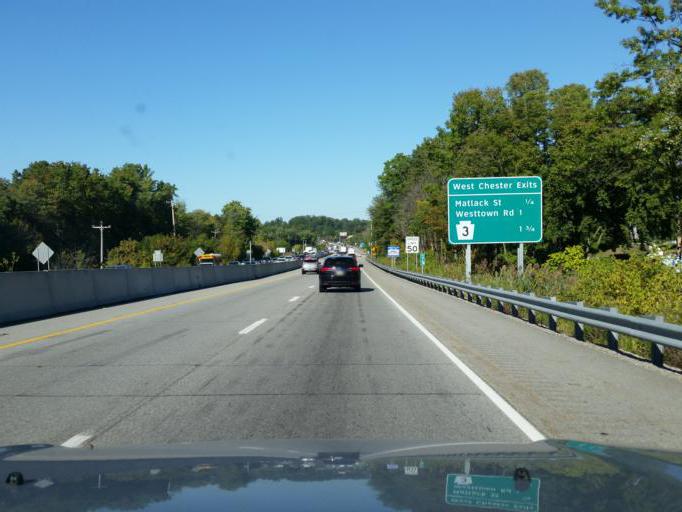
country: US
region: Pennsylvania
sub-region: Chester County
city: West Chester
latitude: 39.9425
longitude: -75.5885
